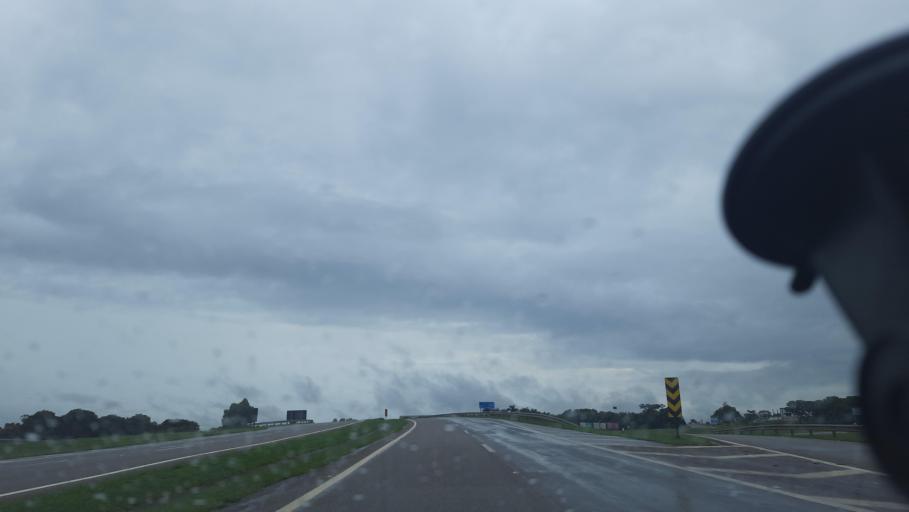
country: BR
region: Sao Paulo
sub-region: Casa Branca
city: Casa Branca
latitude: -21.7844
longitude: -47.0635
